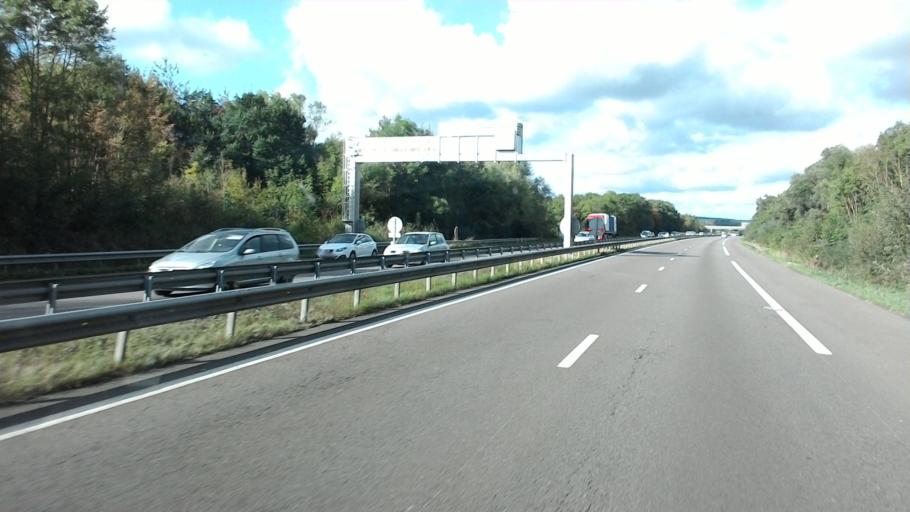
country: FR
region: Lorraine
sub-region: Departement de la Moselle
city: Entrange
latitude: 49.4272
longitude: 6.1124
